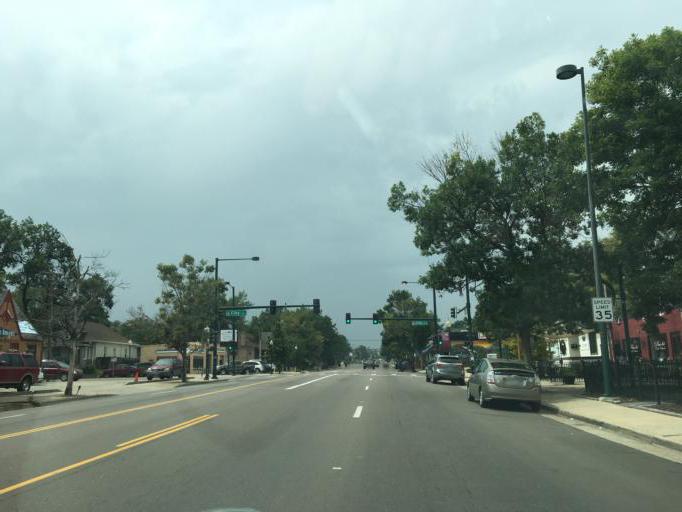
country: US
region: Colorado
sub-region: Adams County
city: Berkley
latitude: 39.7693
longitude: -105.0196
